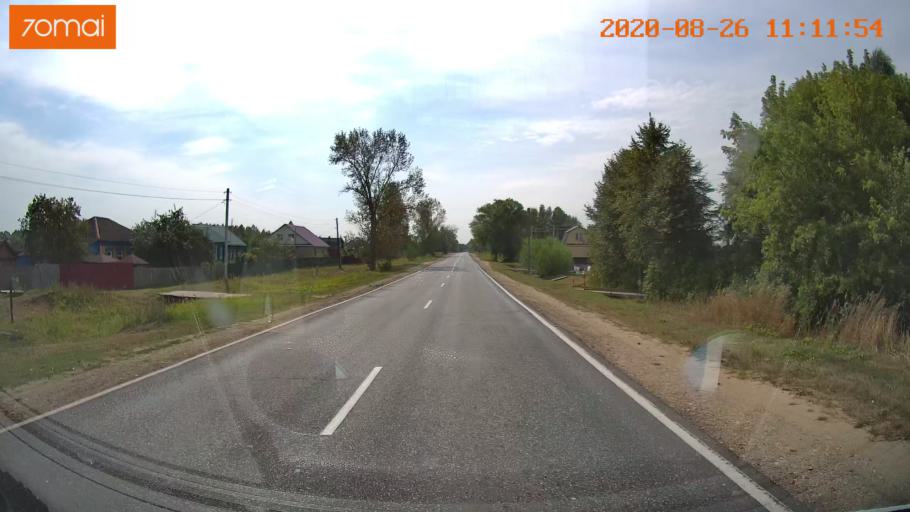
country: RU
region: Rjazan
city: Izhevskoye
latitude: 54.4757
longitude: 41.1259
